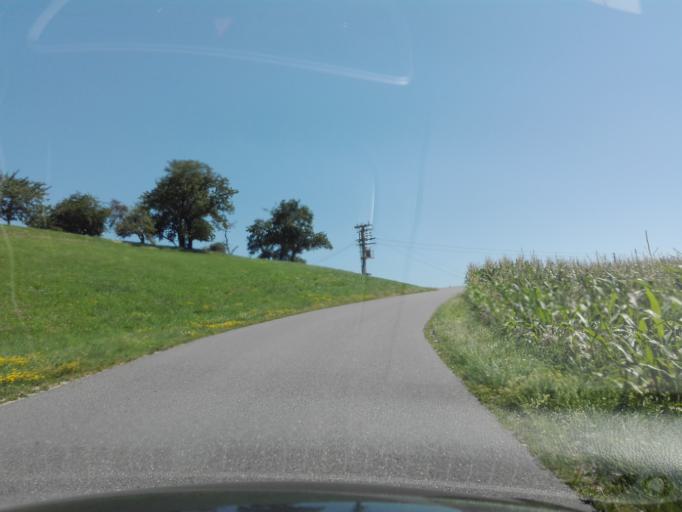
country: AT
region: Upper Austria
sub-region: Politischer Bezirk Urfahr-Umgebung
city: Steyregg
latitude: 48.2942
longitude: 14.3838
